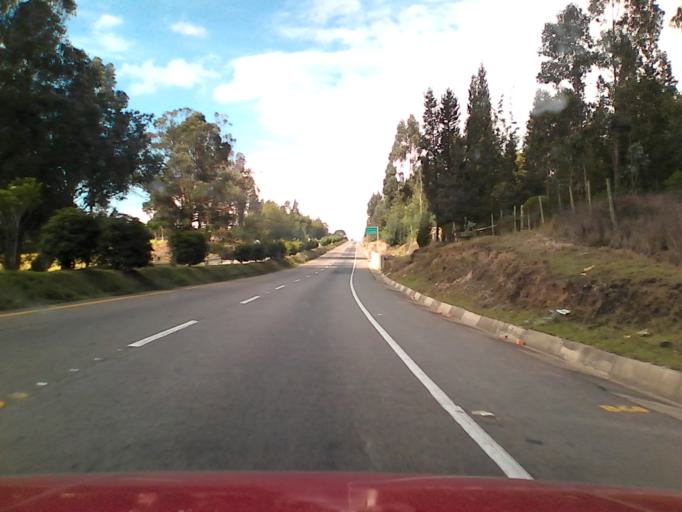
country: CO
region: Boyaca
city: Combita
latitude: 5.6400
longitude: -73.2886
